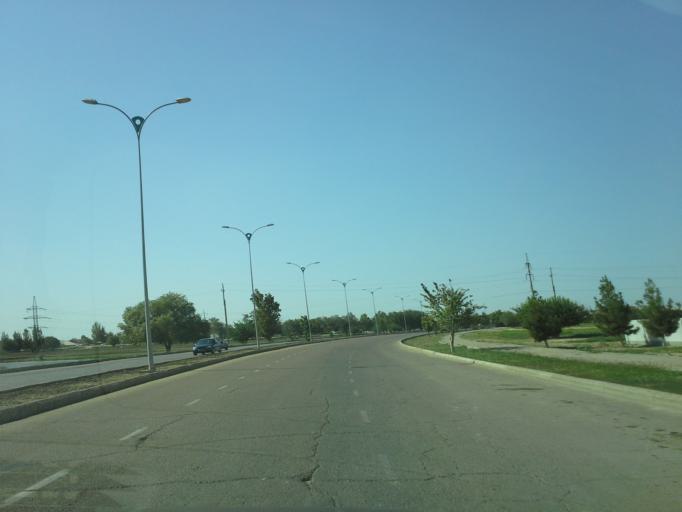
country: TM
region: Dasoguz
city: Dasoguz
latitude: 41.8101
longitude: 59.9950
